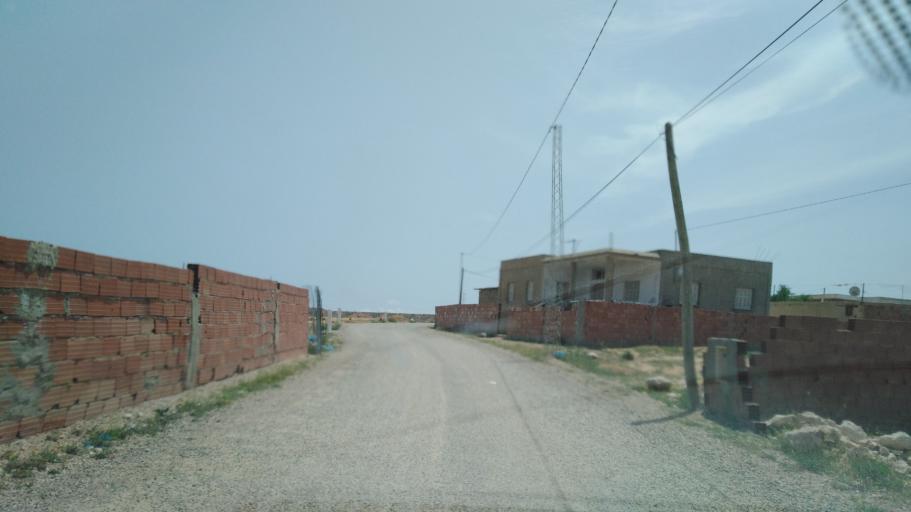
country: TN
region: Safaqis
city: Sfax
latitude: 34.7272
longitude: 10.5538
